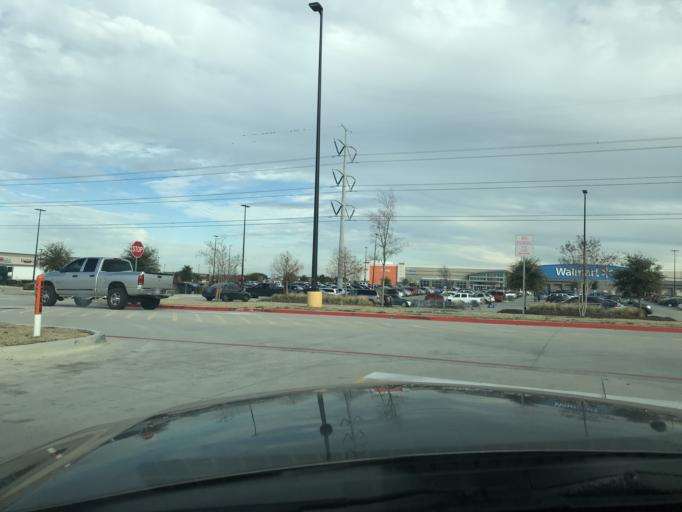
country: US
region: Texas
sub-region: Dallas County
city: Grand Prairie
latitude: 32.7072
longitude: -97.0233
